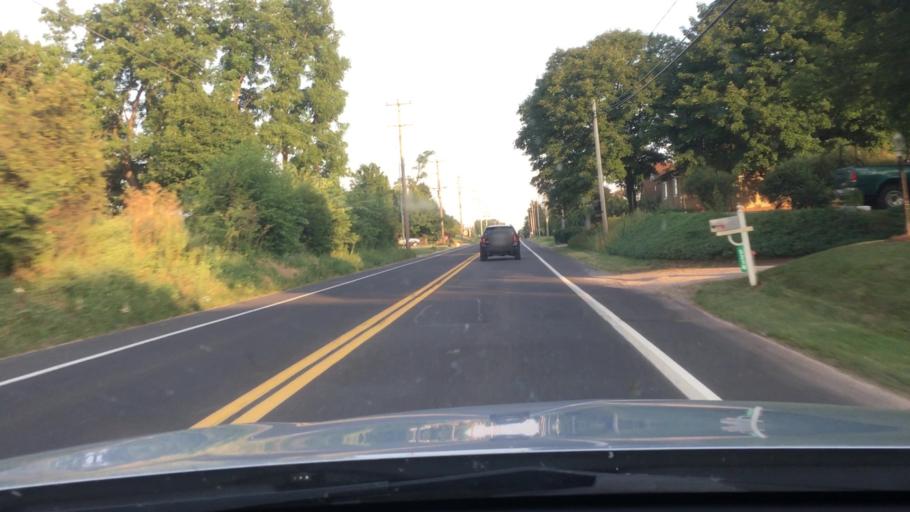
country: US
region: Pennsylvania
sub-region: York County
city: Dover
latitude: 40.0165
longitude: -76.8646
